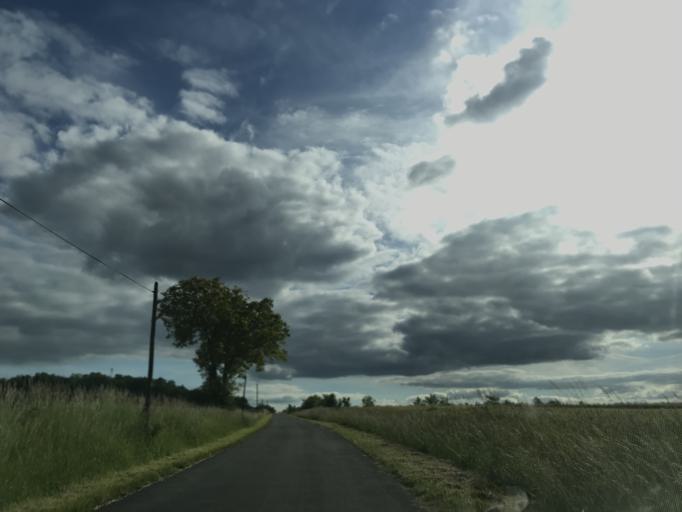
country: FR
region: Aquitaine
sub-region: Departement de la Dordogne
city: Saint-Aulaye
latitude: 45.2492
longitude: 0.1207
